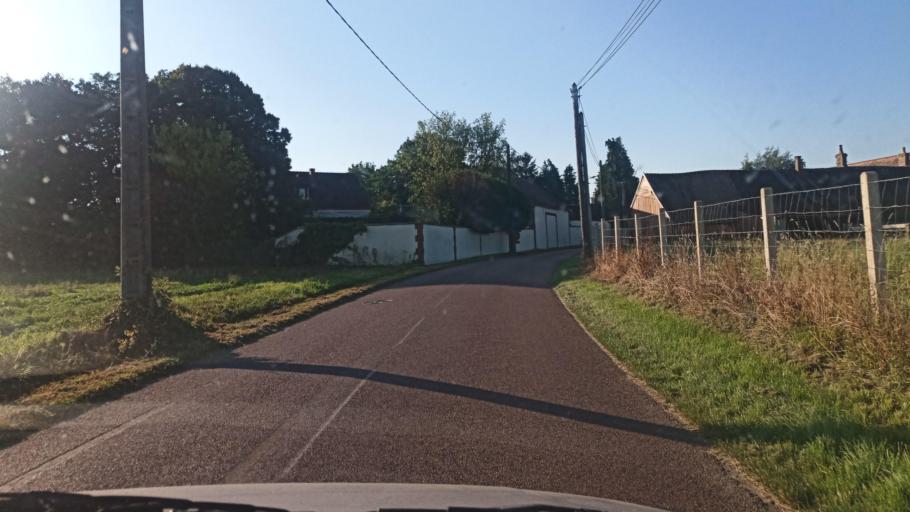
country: FR
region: Bourgogne
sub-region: Departement de l'Yonne
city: Saint-Valerien
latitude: 48.1947
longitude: 3.1205
